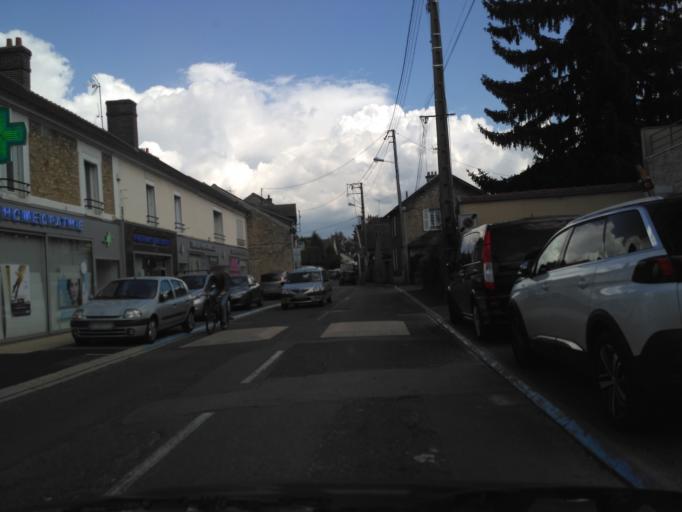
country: FR
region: Ile-de-France
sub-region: Departement de Seine-et-Marne
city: Cesson
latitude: 48.5628
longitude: 2.6050
